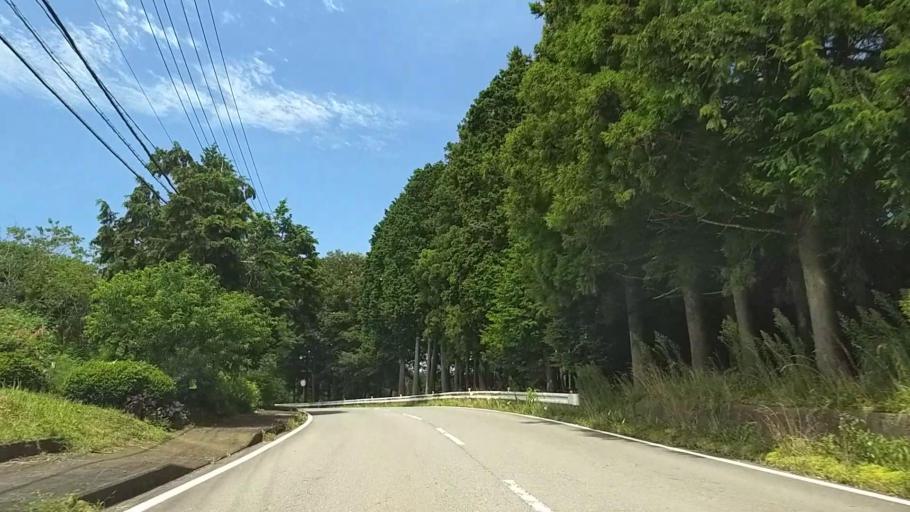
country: JP
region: Shizuoka
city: Gotemba
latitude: 35.2409
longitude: 138.8709
